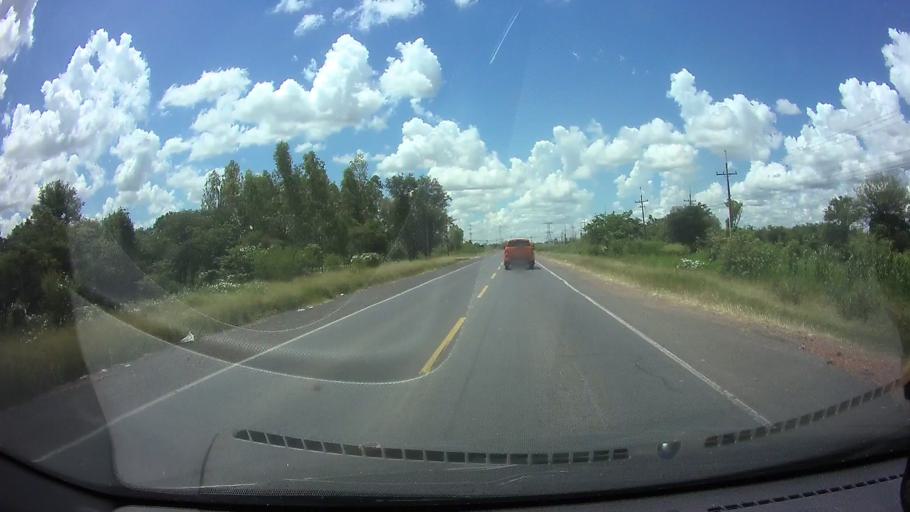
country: PY
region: Central
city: Colonia Mariano Roque Alonso
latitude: -25.1819
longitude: -57.5896
